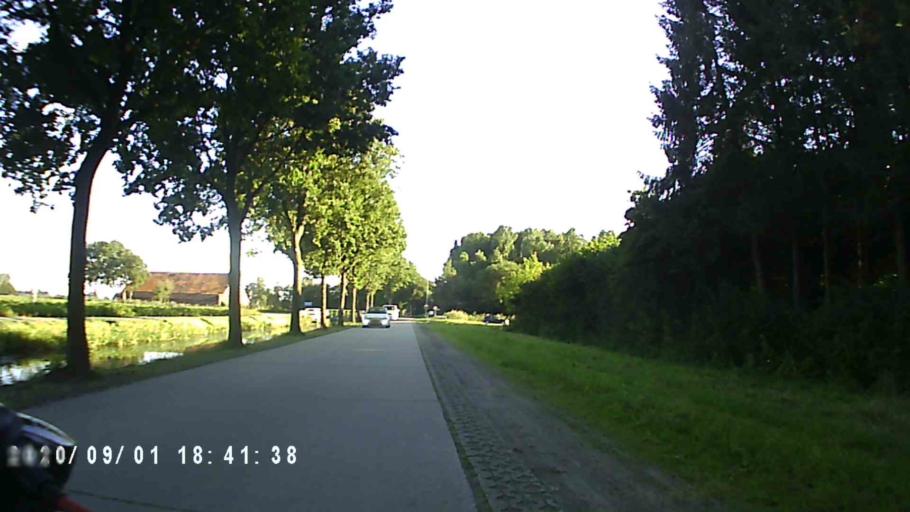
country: NL
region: Groningen
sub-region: Gemeente Hoogezand-Sappemeer
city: Sappemeer
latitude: 53.1472
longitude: 6.8240
